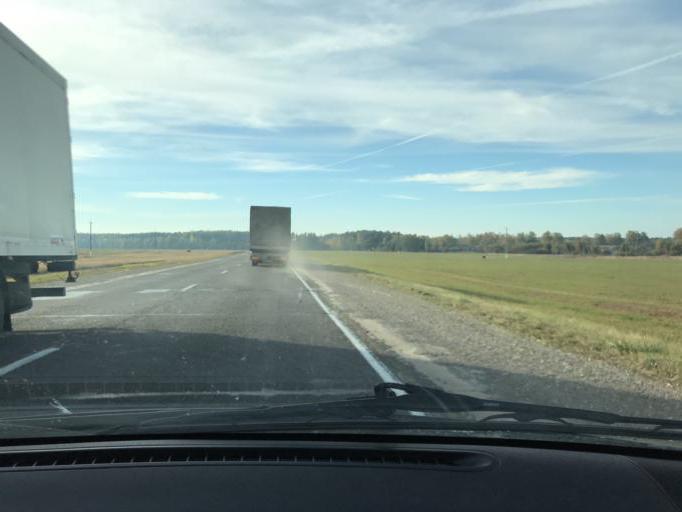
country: BY
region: Brest
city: Horad Pinsk
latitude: 52.1499
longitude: 25.8633
